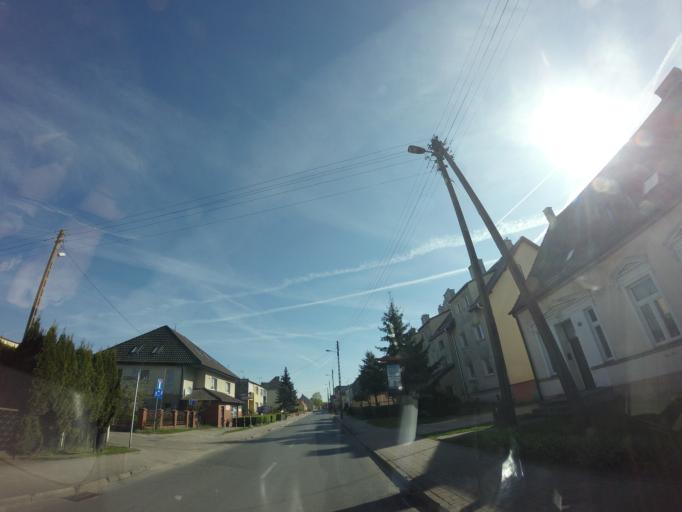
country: PL
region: West Pomeranian Voivodeship
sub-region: Powiat choszczenski
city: Drawno
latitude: 53.2171
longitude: 15.7539
